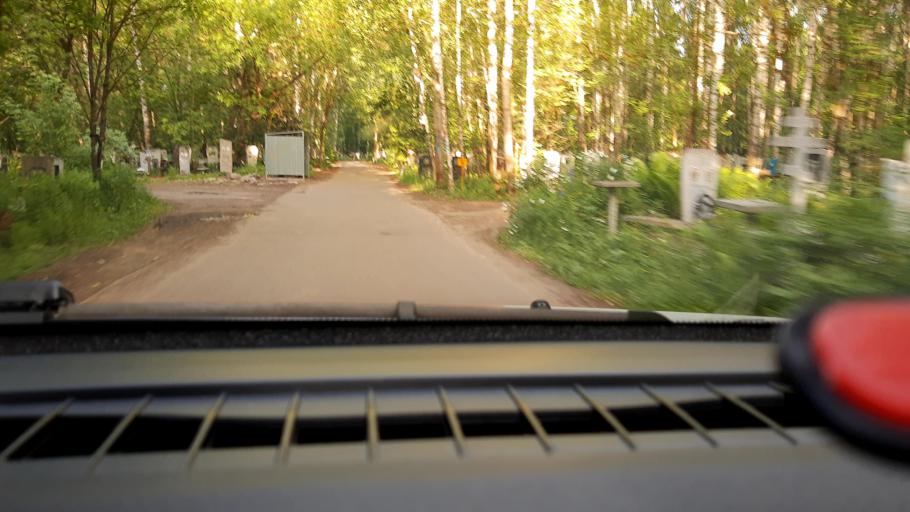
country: RU
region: Nizjnij Novgorod
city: Gorbatovka
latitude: 56.2324
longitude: 43.7668
